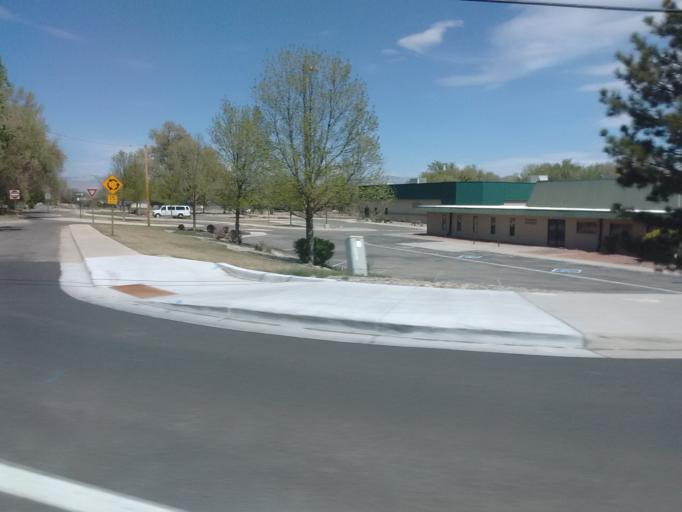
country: US
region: Colorado
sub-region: Mesa County
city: Redlands
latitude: 39.0854
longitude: -108.6484
